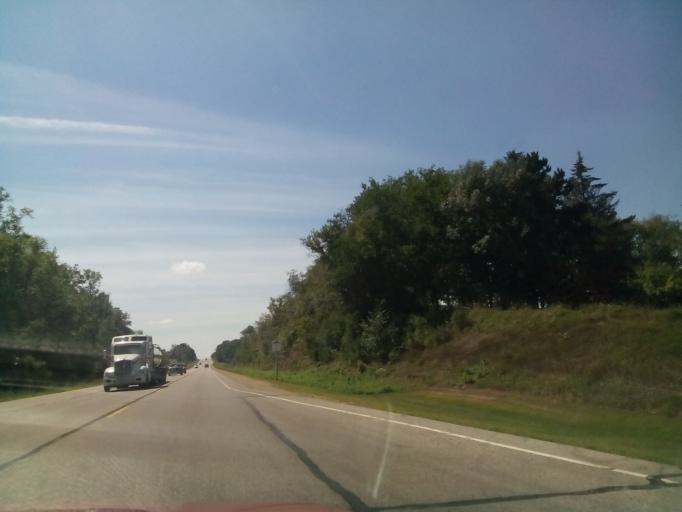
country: US
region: Wisconsin
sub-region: Green County
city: Monticello
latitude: 42.7420
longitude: -89.5992
